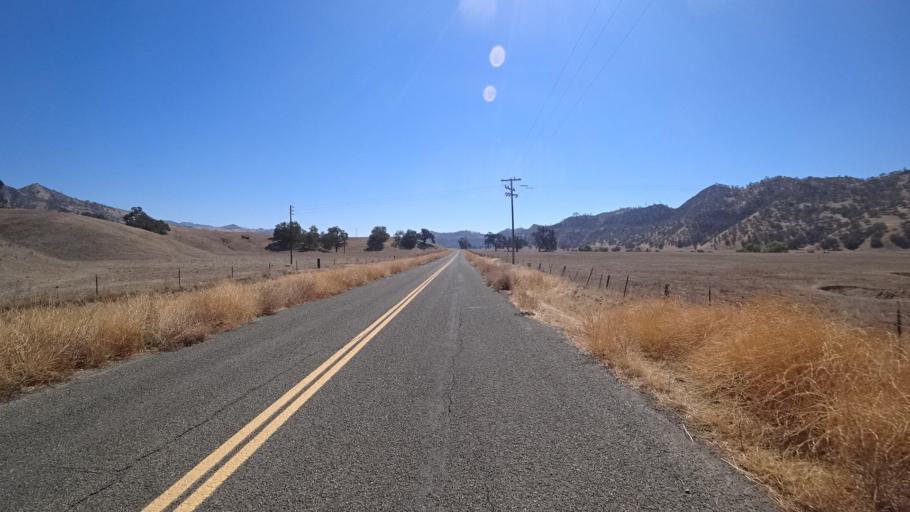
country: US
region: California
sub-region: Monterey County
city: King City
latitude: 36.1763
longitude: -120.7962
